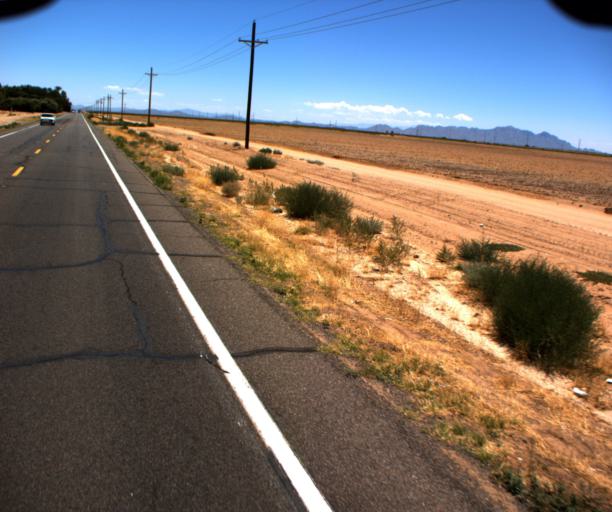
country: US
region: Arizona
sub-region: Pinal County
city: Casa Grande
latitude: 32.8798
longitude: -111.6334
